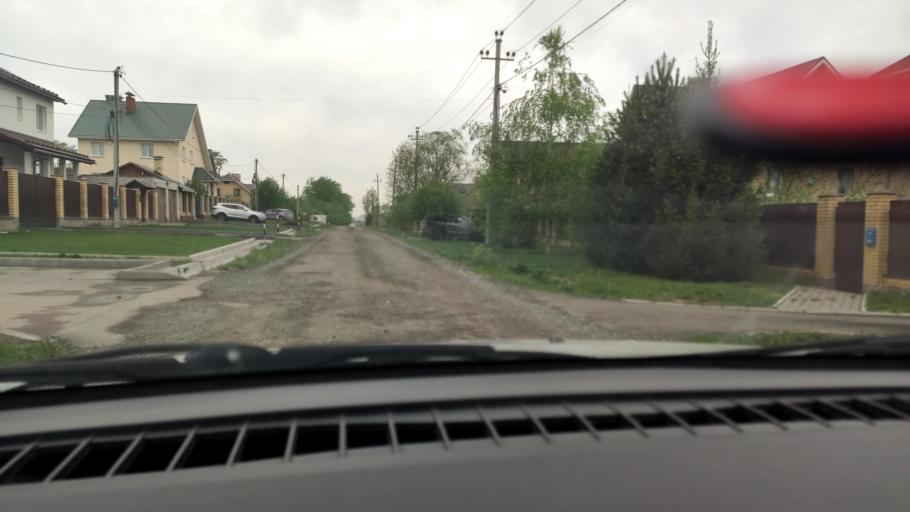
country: RU
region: Perm
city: Perm
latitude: 57.9964
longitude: 56.3412
